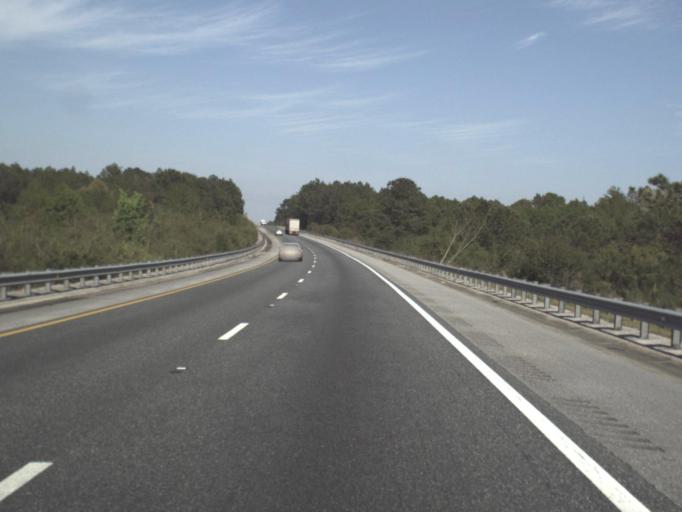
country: US
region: Florida
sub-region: Okaloosa County
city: Crestview
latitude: 30.7134
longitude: -86.6230
